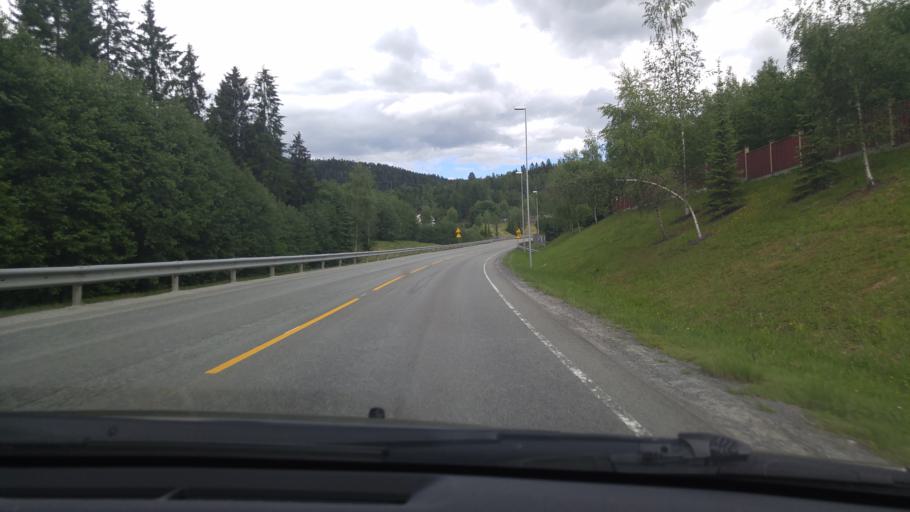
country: NO
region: Nord-Trondelag
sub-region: Steinkjer
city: Steinkjer
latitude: 64.0342
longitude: 11.4731
